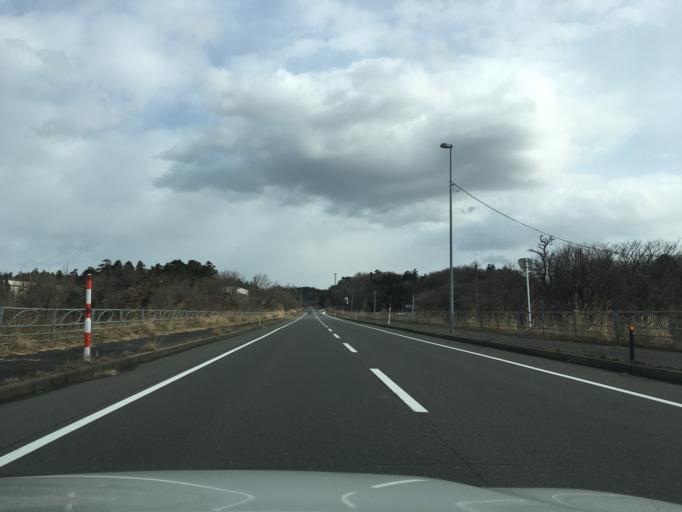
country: JP
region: Yamagata
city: Yuza
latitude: 39.2453
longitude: 139.9220
